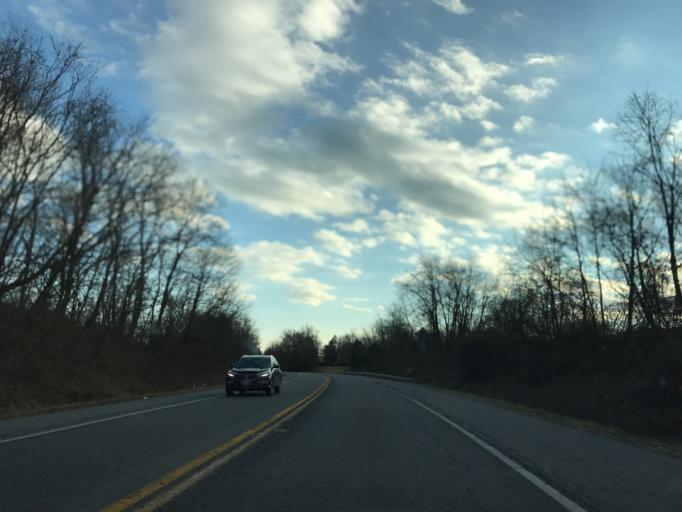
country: US
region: Maryland
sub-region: Cecil County
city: North East
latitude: 39.6458
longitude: -75.9583
